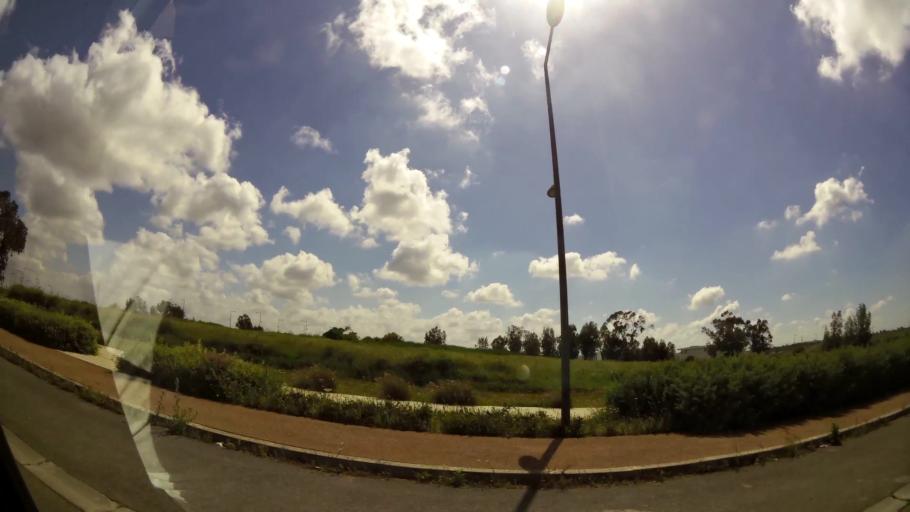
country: MA
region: Grand Casablanca
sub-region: Nouaceur
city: Bouskoura
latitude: 33.4969
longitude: -7.6068
